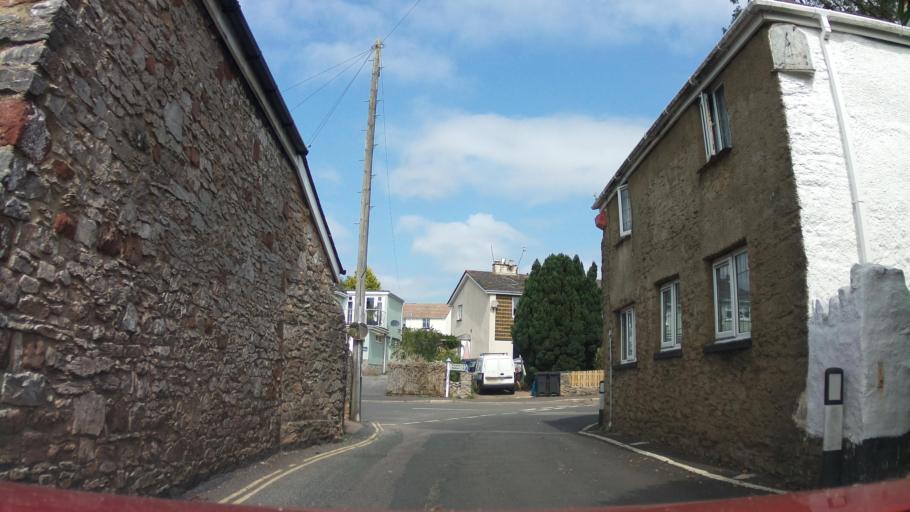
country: GB
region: England
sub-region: Devon
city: Marldon
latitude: 50.4063
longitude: -3.6242
